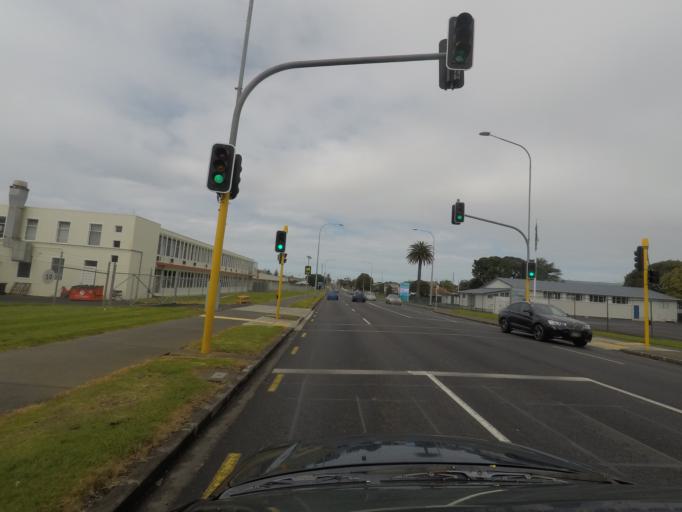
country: NZ
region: Auckland
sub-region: Auckland
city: Tamaki
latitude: -36.9011
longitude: 174.8433
